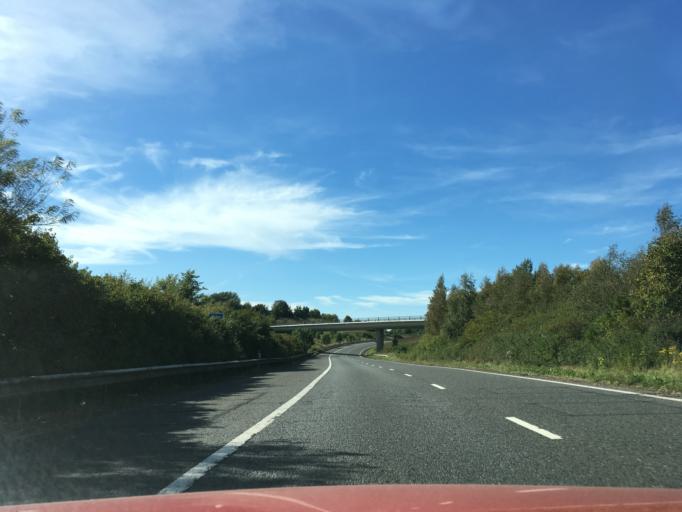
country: GB
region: England
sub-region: South Gloucestershire
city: Almondsbury
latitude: 51.5699
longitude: -2.5786
